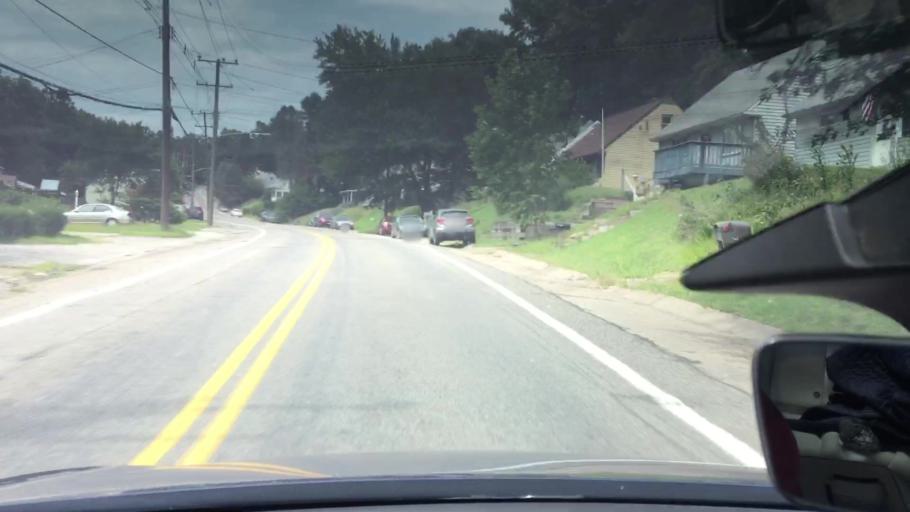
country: US
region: Pennsylvania
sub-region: Allegheny County
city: Churchill
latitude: 40.4541
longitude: -79.8137
